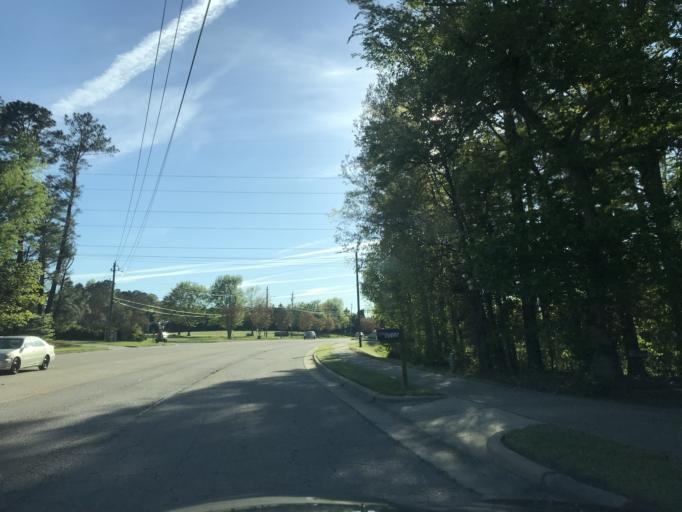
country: US
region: North Carolina
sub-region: Wake County
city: Knightdale
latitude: 35.8317
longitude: -78.5627
